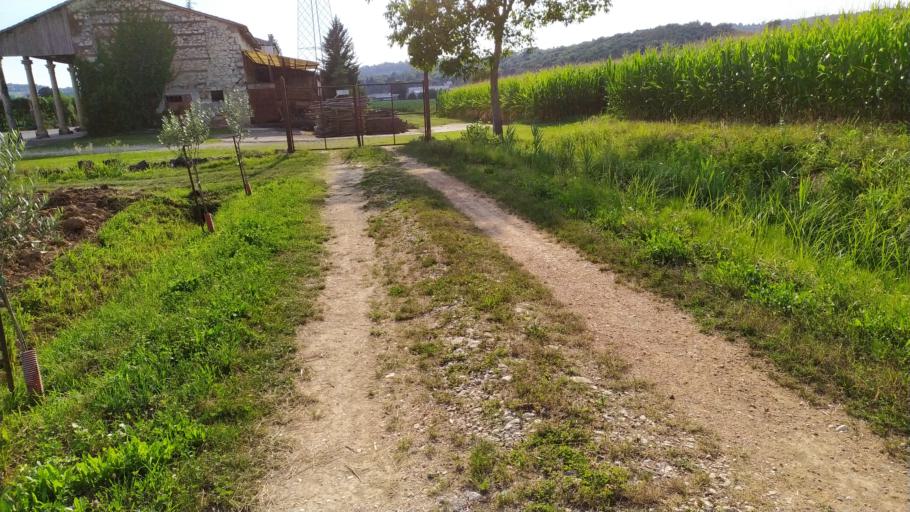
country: IT
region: Veneto
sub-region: Provincia di Vicenza
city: Costabissara
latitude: 45.5676
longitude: 11.4869
